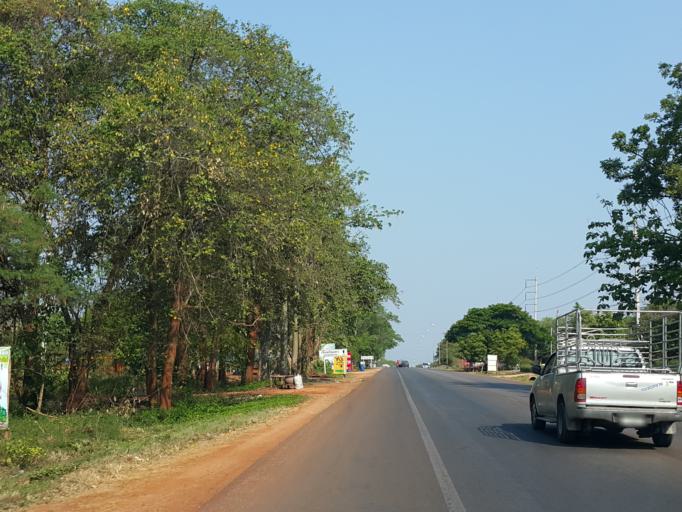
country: TH
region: Kanchanaburi
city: Sai Yok
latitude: 14.1253
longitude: 99.1724
